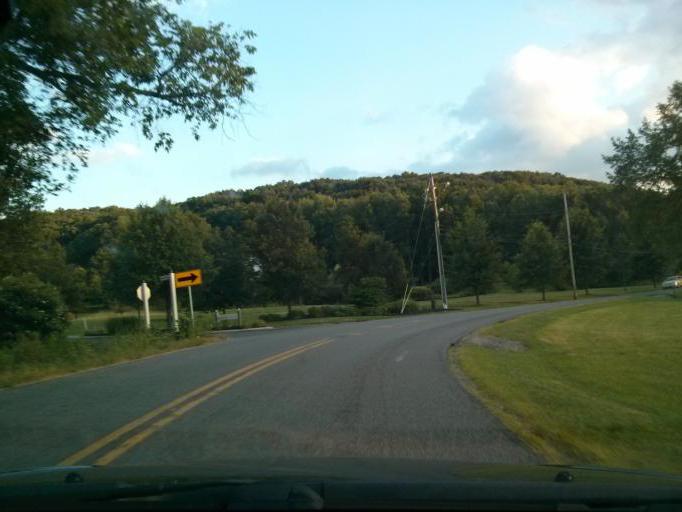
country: US
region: Pennsylvania
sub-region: Centre County
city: Park Forest Village
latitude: 40.8287
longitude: -77.9365
